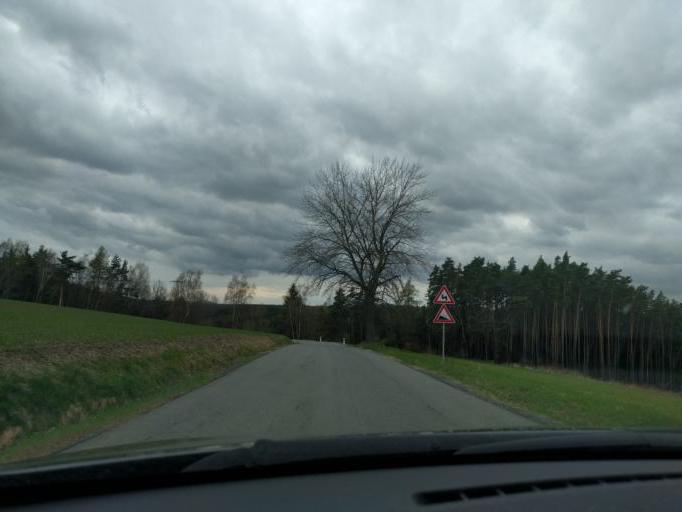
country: CZ
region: Plzensky
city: Bezdruzice
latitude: 49.9214
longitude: 13.0375
